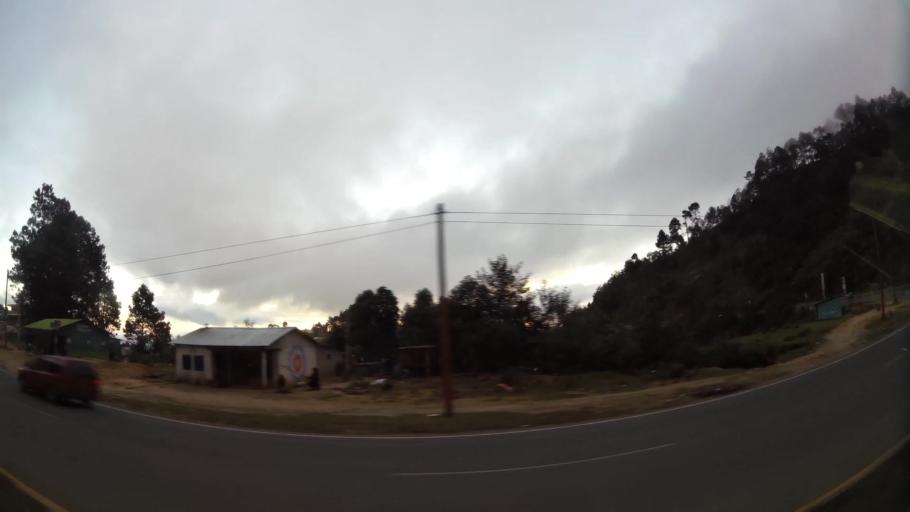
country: GT
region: Solola
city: Concepcion
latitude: 14.8484
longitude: -91.1348
